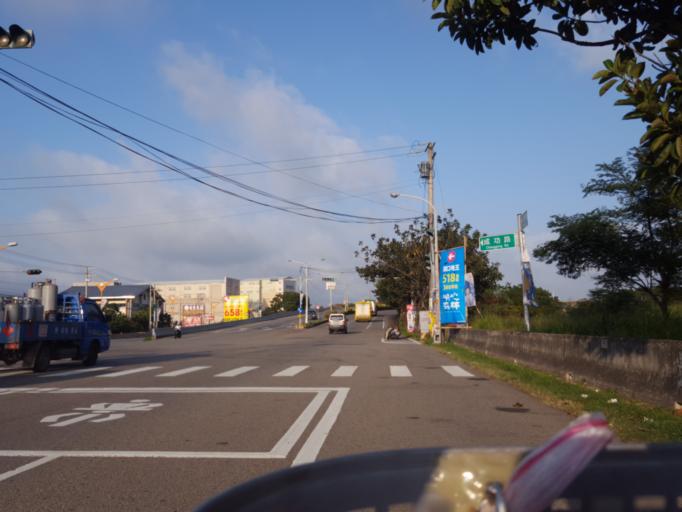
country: TW
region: Taiwan
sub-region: Hsinchu
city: Zhubei
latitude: 24.8850
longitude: 121.0143
